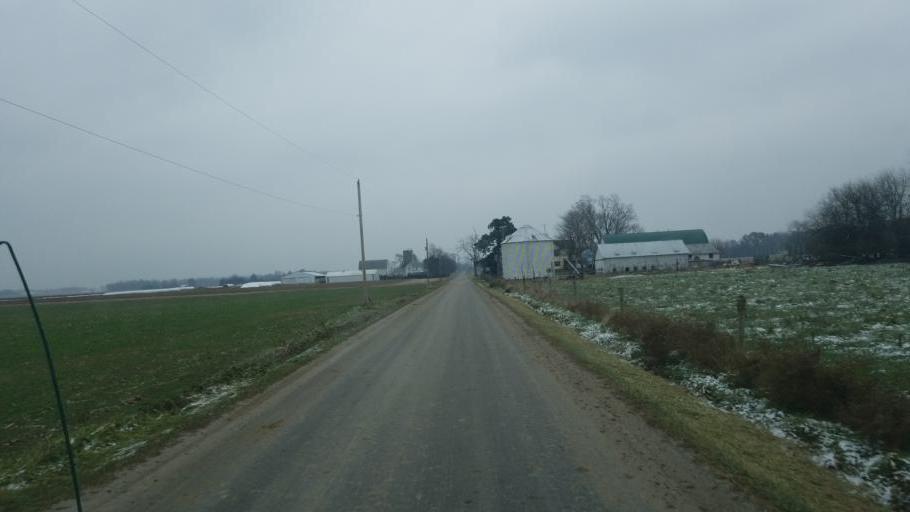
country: US
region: Ohio
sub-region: Richland County
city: Shelby
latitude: 40.9304
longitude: -82.6810
